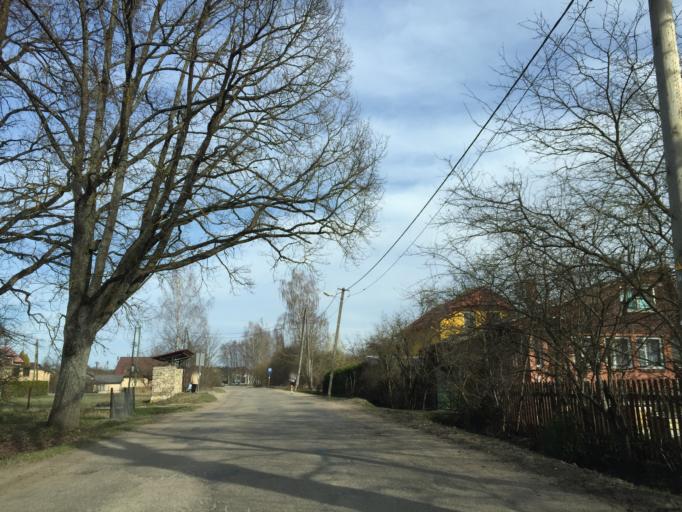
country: LV
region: Ogre
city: Ogre
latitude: 56.8098
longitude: 24.6415
